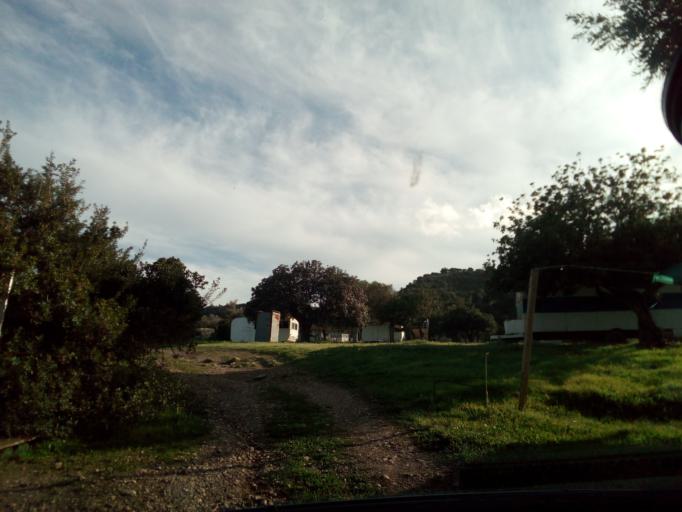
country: CY
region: Pafos
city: Polis
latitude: 35.0587
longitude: 32.3454
